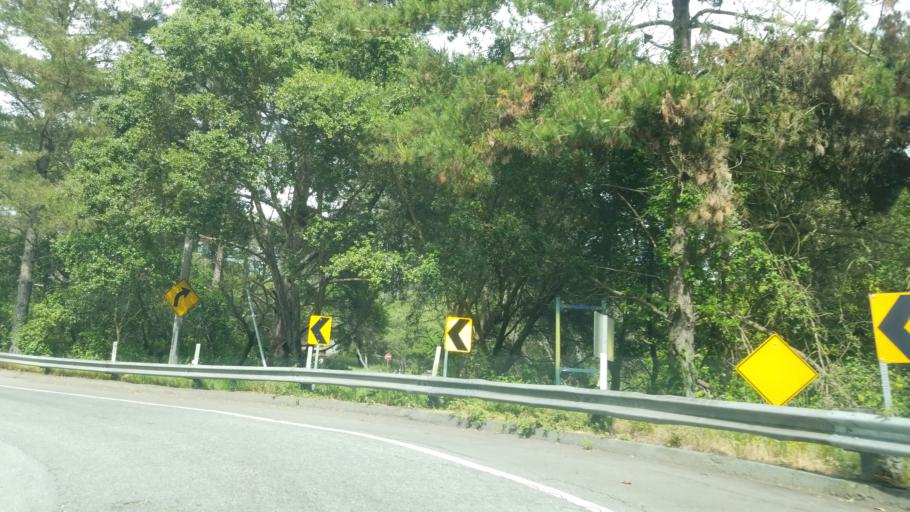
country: US
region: California
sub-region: Santa Cruz County
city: Capitola
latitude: 36.9823
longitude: -121.9375
